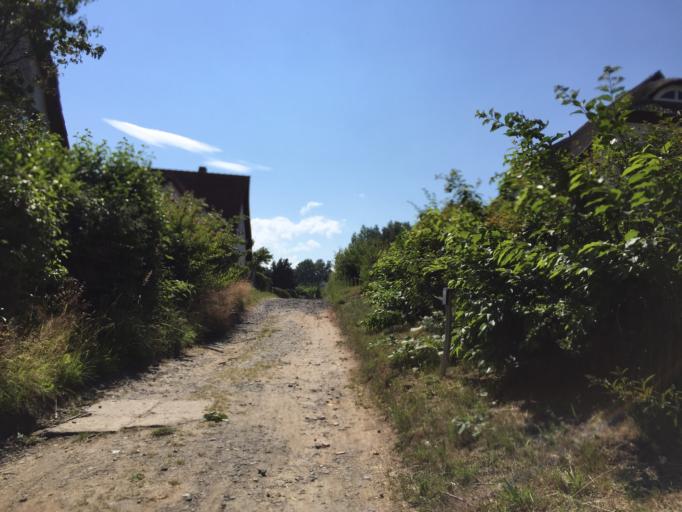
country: DE
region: Mecklenburg-Vorpommern
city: Hiddensee
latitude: 54.5877
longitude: 13.1068
